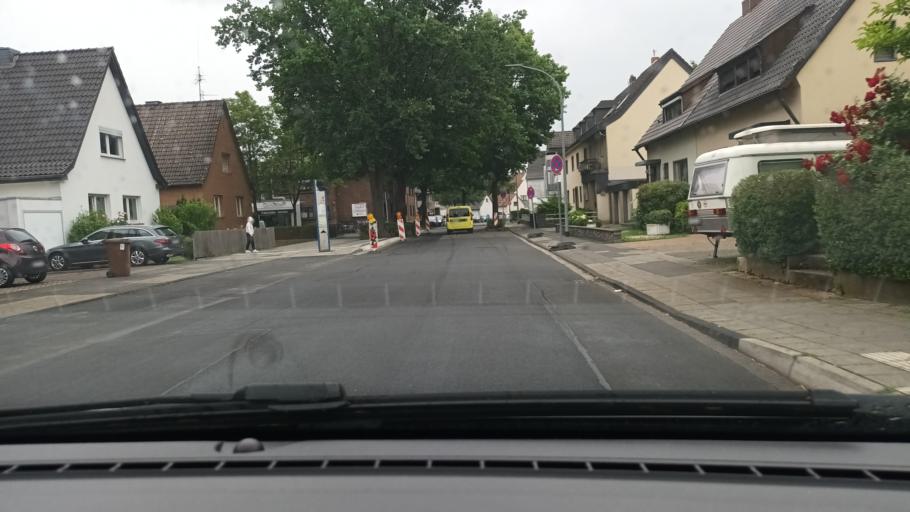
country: DE
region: North Rhine-Westphalia
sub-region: Regierungsbezirk Koln
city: Hurth
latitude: 50.8966
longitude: 6.8908
